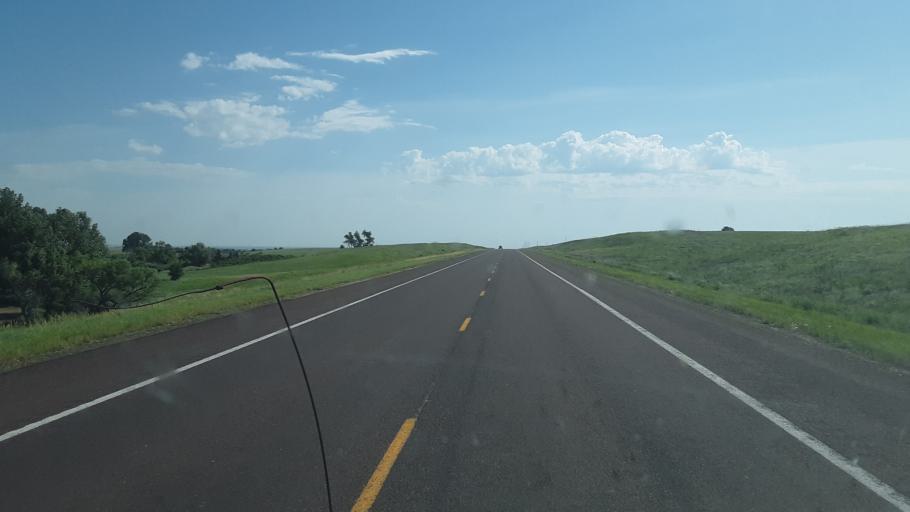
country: US
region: Kansas
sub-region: Ellsworth County
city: Ellsworth
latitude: 38.6360
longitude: -98.3458
